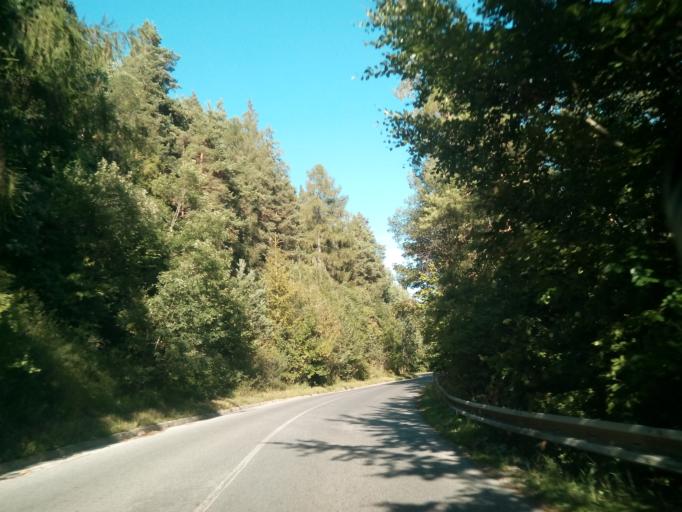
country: SK
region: Presovsky
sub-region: Okres Poprad
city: Svit
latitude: 49.0075
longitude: 20.2406
